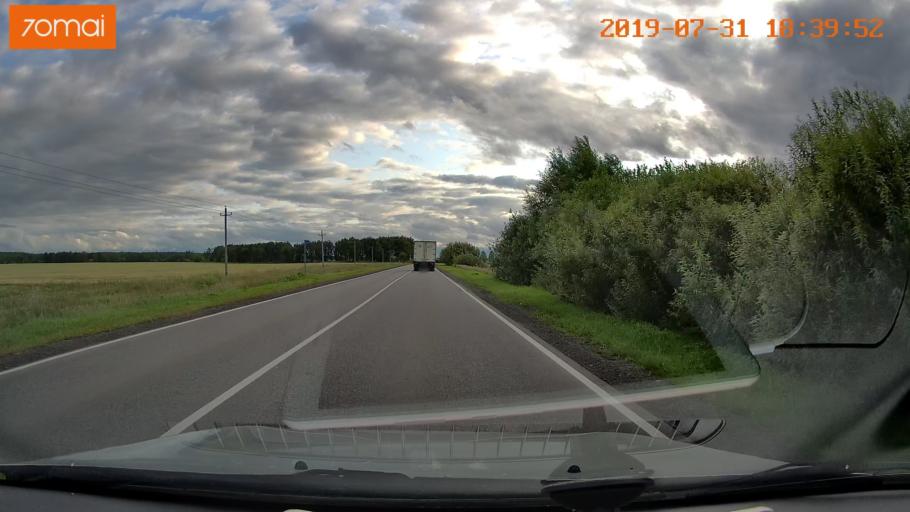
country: RU
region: Moskovskaya
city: Voskresensk
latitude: 55.2645
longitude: 38.6395
